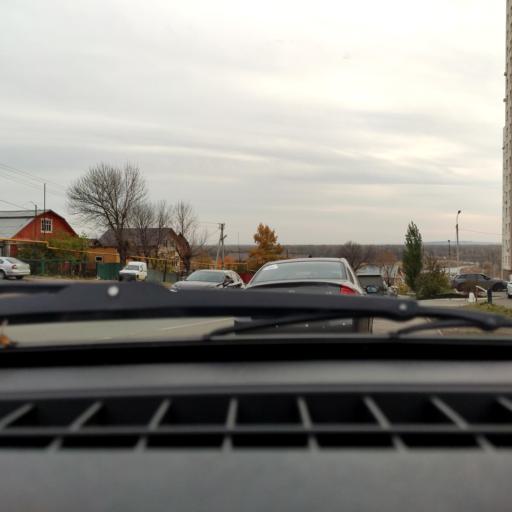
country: RU
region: Bashkortostan
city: Ufa
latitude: 54.6884
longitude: 55.9975
